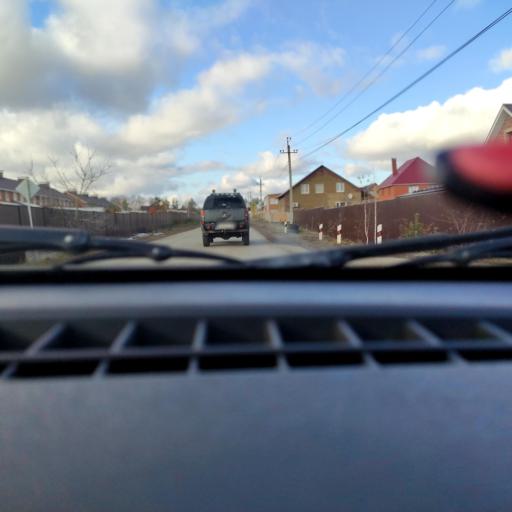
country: RU
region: Bashkortostan
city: Ufa
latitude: 54.6000
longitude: 55.9226
